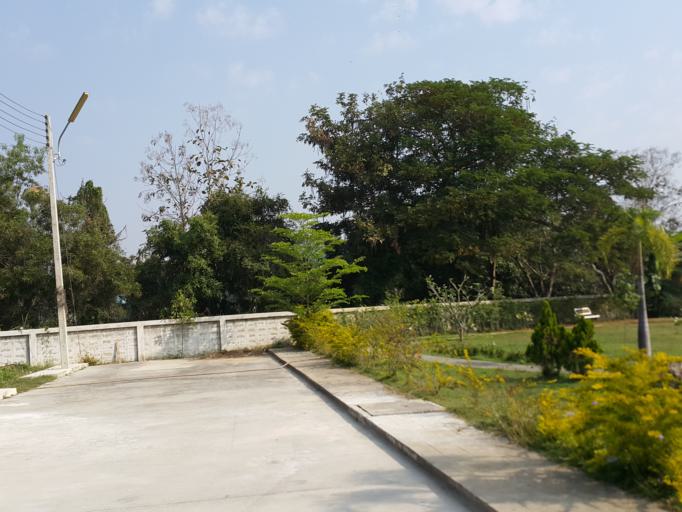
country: TH
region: Chiang Mai
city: San Kamphaeng
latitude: 18.7826
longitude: 99.0907
